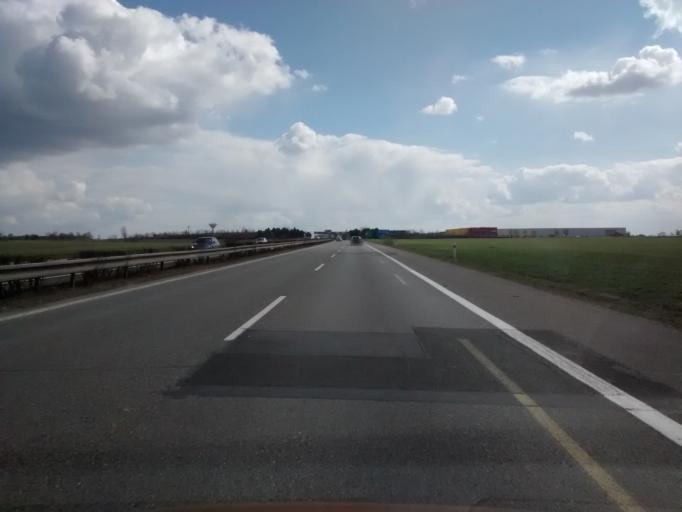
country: CZ
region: Central Bohemia
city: Zdiby
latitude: 50.1902
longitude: 14.4434
